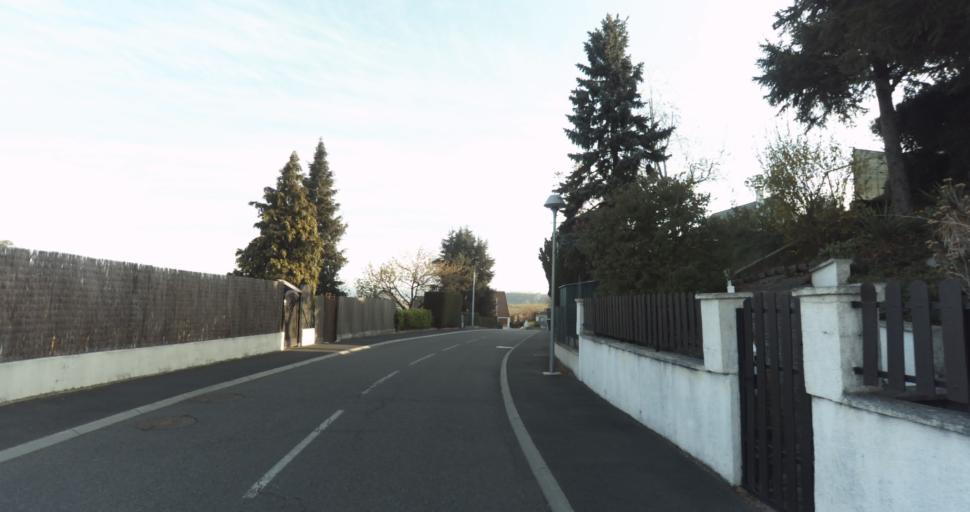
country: FR
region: Rhone-Alpes
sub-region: Departement de la Loire
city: Saint-Jean-Bonnefonds
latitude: 45.4515
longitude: 4.4287
